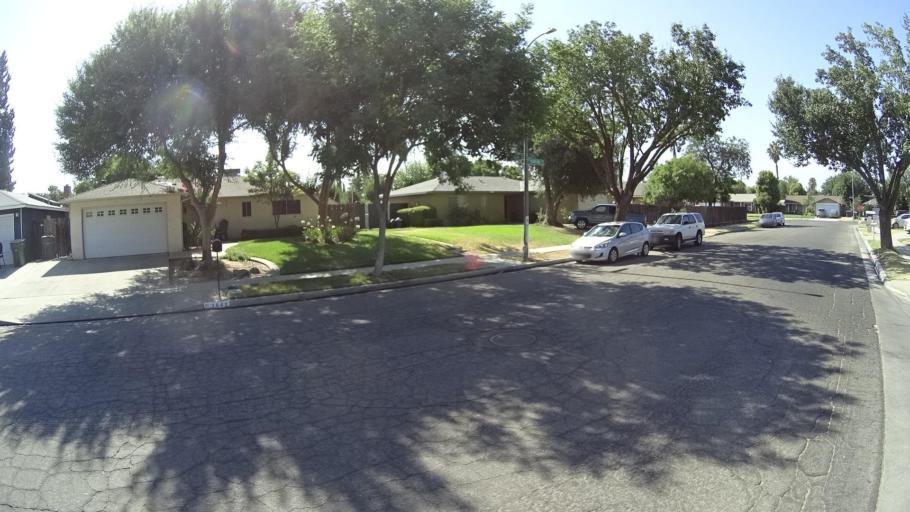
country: US
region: California
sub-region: Fresno County
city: Tarpey Village
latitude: 36.7876
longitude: -119.6870
